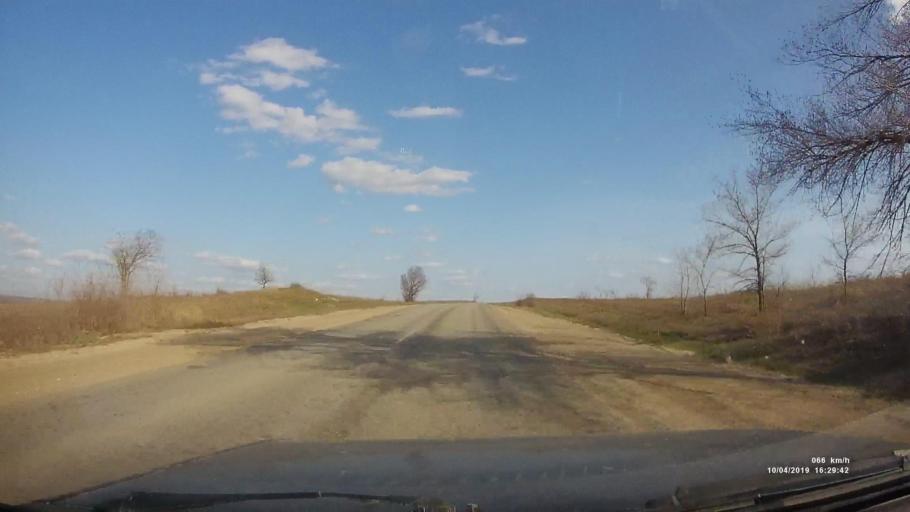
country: RU
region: Rostov
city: Staraya Stanitsa
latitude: 48.2670
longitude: 40.3581
